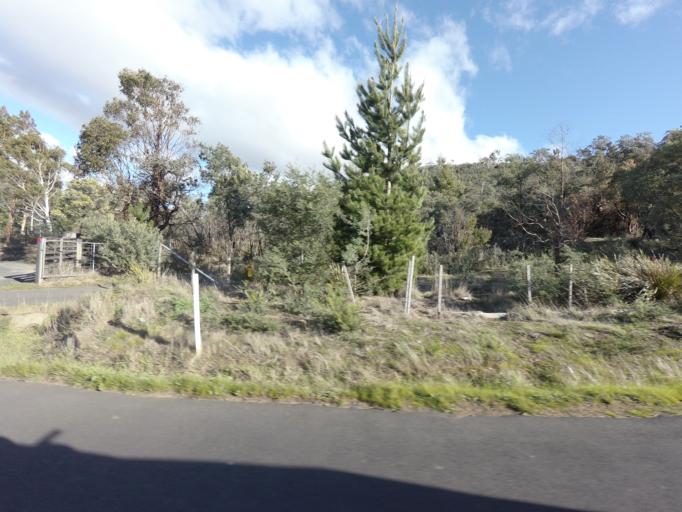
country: AU
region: Tasmania
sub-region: Derwent Valley
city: New Norfolk
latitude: -42.7476
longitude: 147.0444
